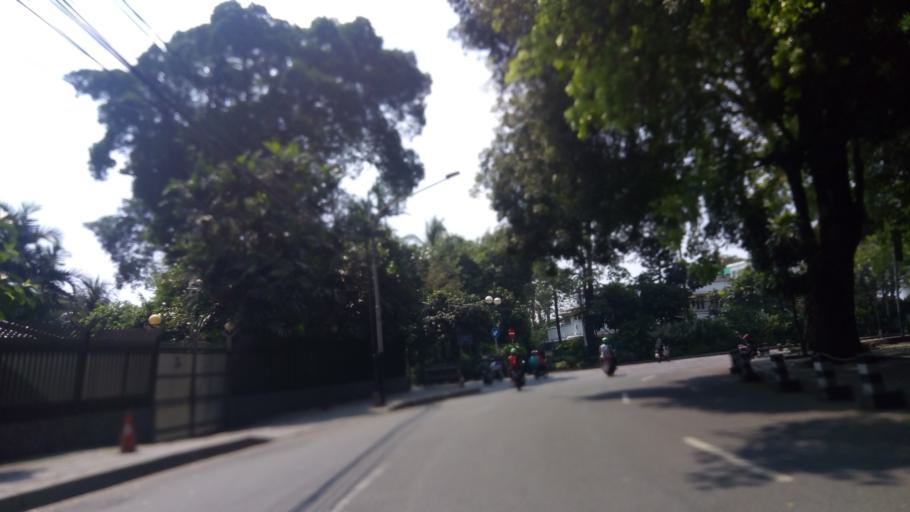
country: ID
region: Jakarta Raya
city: Jakarta
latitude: -6.1989
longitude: 106.8320
